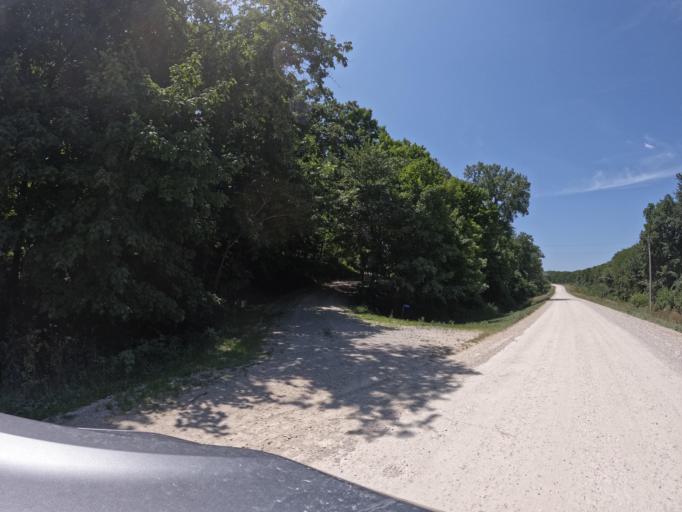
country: US
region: Iowa
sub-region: Henry County
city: Mount Pleasant
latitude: 40.9270
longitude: -91.6315
